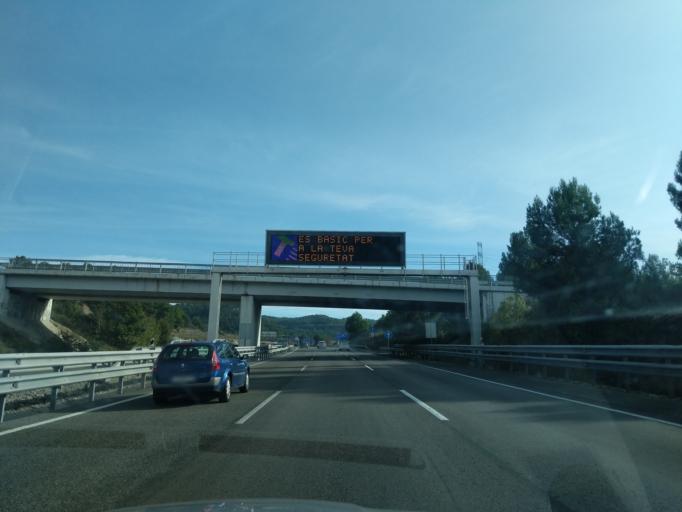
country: ES
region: Catalonia
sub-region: Provincia de Barcelona
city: Castelloli
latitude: 41.5980
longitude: 1.7106
